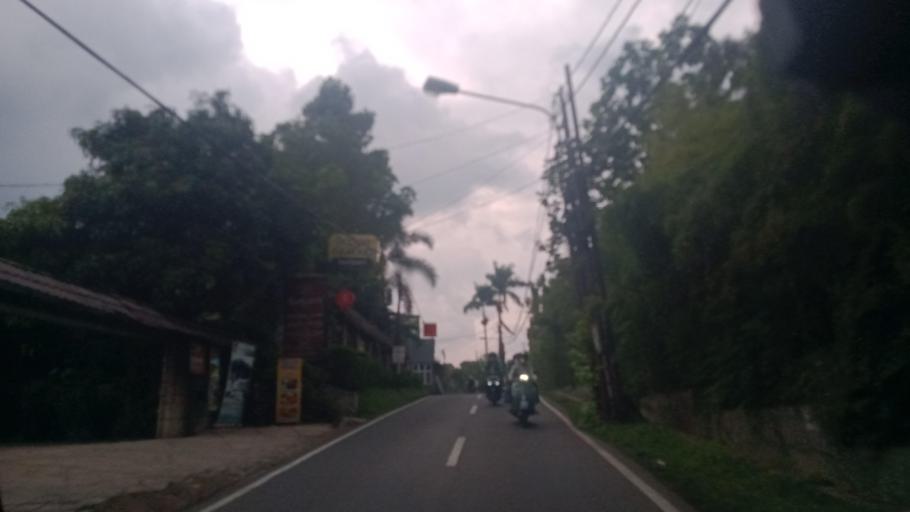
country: ID
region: West Java
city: Lembang
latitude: -6.8550
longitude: 107.5920
